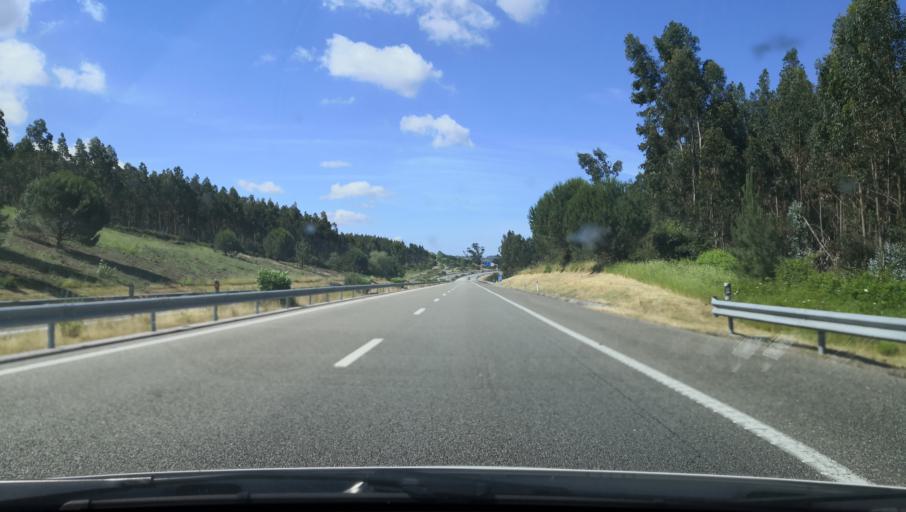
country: PT
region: Coimbra
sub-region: Montemor-O-Velho
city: Montemor-o-Velho
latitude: 40.1803
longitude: -8.7053
